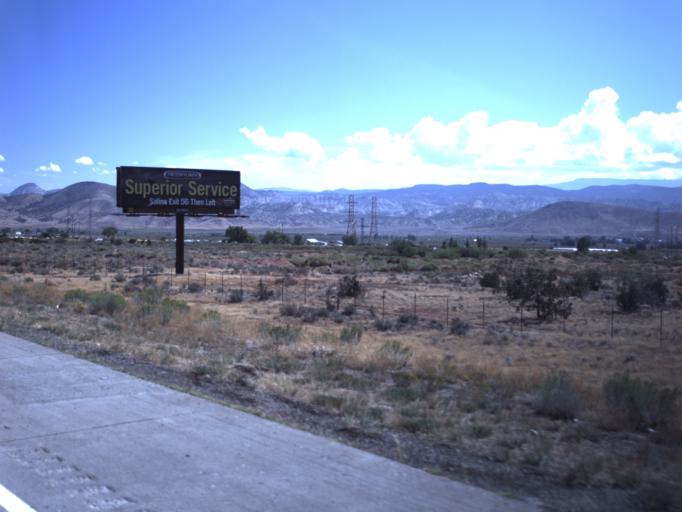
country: US
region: Utah
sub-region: Sevier County
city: Aurora
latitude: 38.8510
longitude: -112.0013
